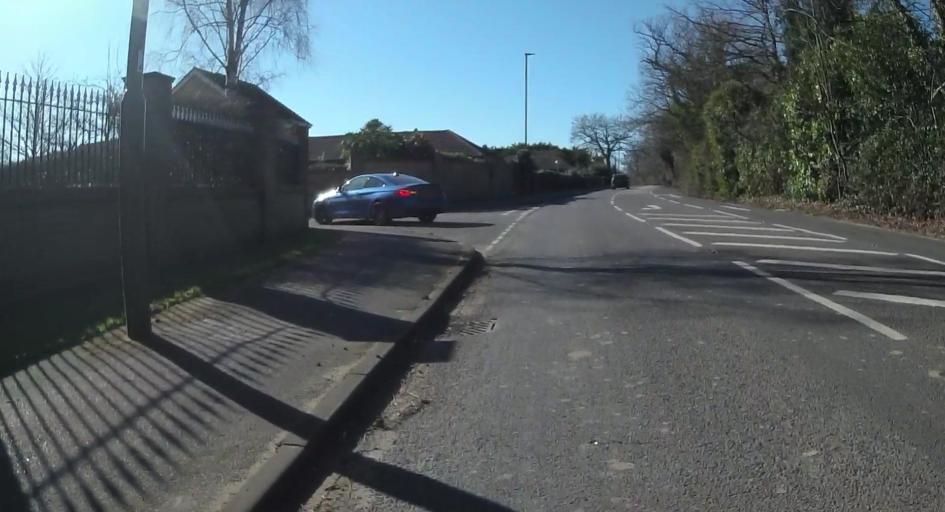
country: GB
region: England
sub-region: Surrey
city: Ottershaw
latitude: 51.3658
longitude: -0.5255
